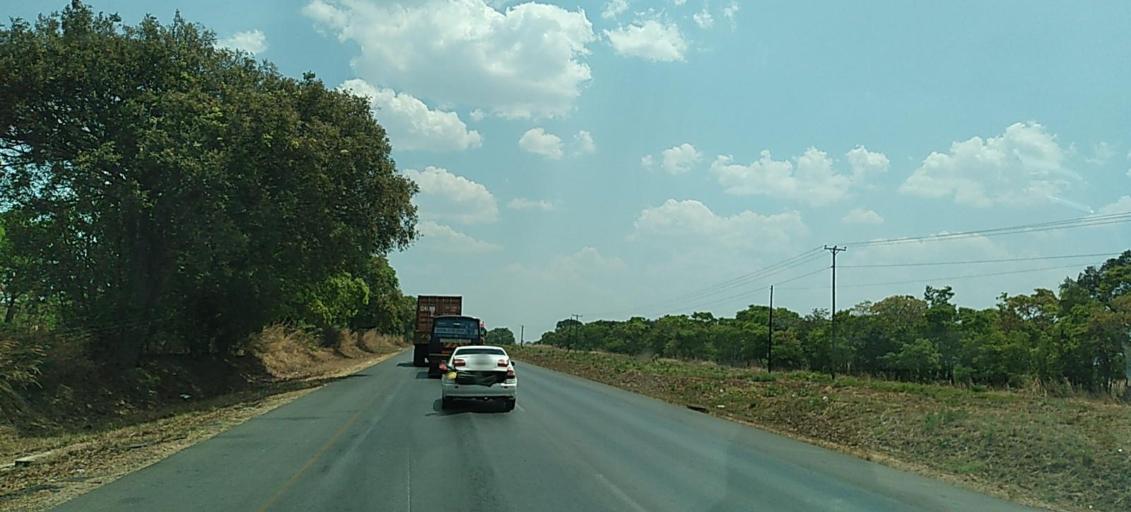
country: ZM
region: Central
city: Kabwe
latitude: -14.3341
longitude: 28.5340
